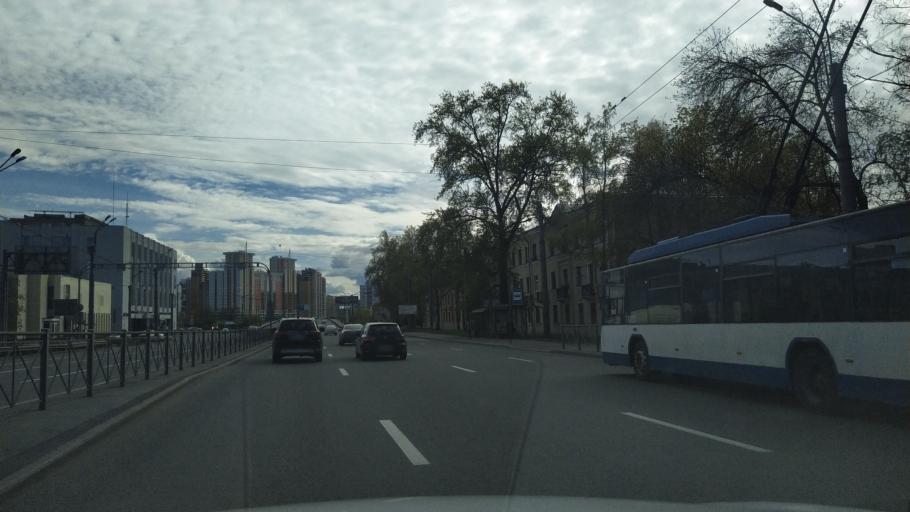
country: RU
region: Leningrad
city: Kalininskiy
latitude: 59.9958
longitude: 30.3802
